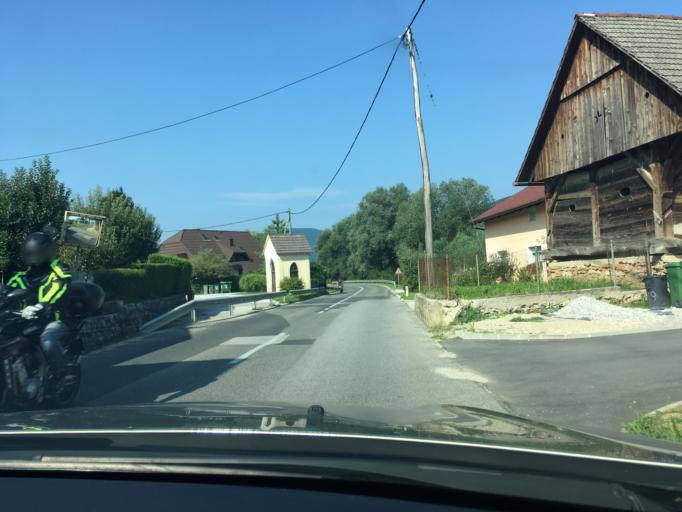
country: SI
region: Straza
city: Straza
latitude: 45.7851
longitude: 15.1012
